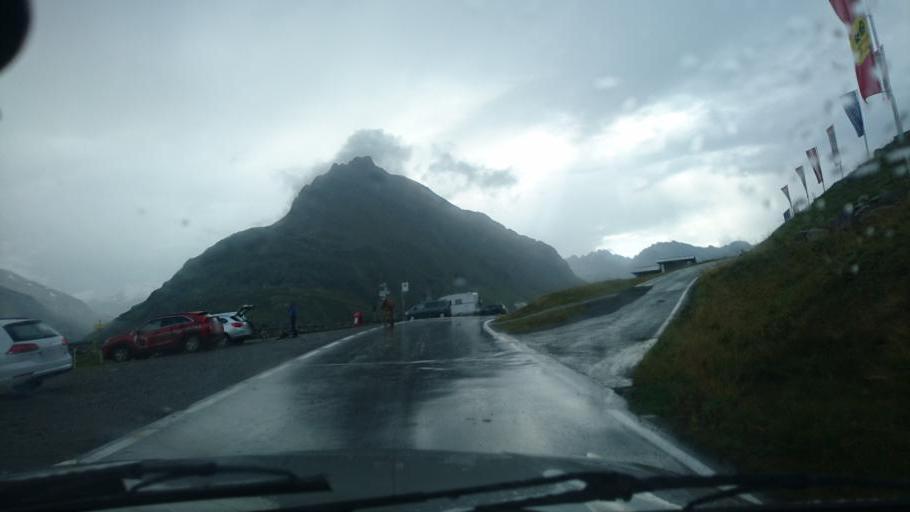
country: AT
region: Vorarlberg
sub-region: Politischer Bezirk Bludenz
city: Gaschurn
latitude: 46.9185
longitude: 10.0975
